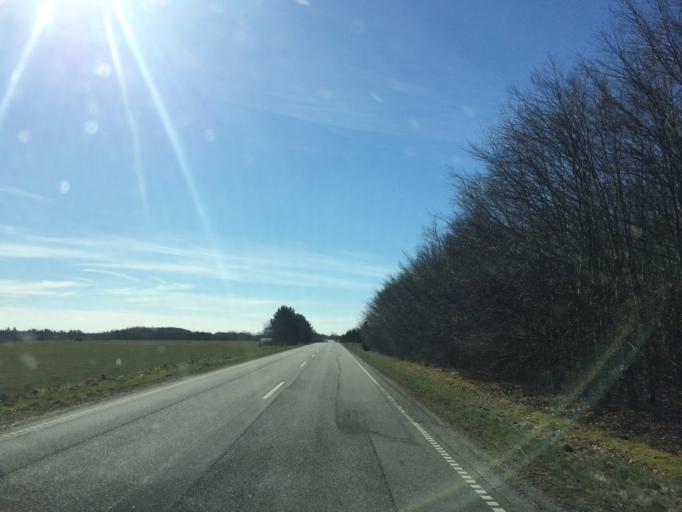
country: DK
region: Central Jutland
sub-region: Lemvig Kommune
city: Lemvig
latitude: 56.4580
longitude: 8.2954
